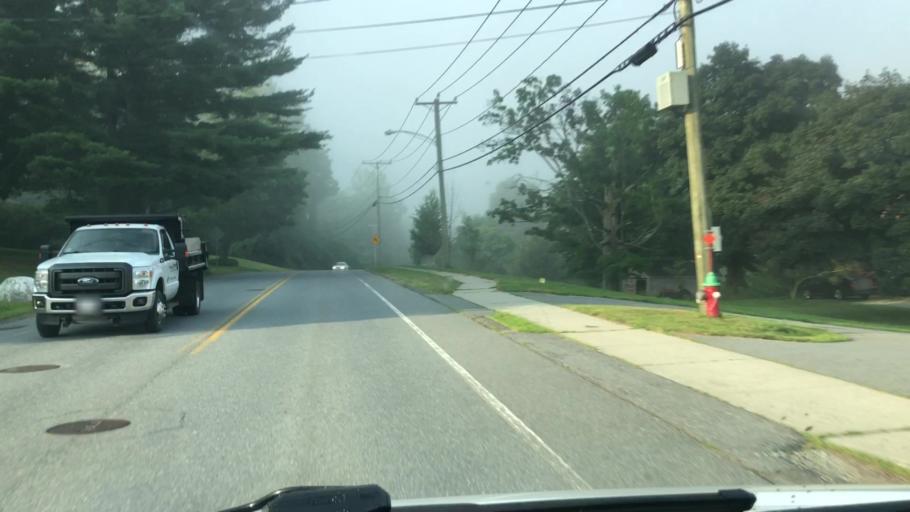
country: US
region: Massachusetts
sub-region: Berkshire County
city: Dalton
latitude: 42.4565
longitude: -73.1826
